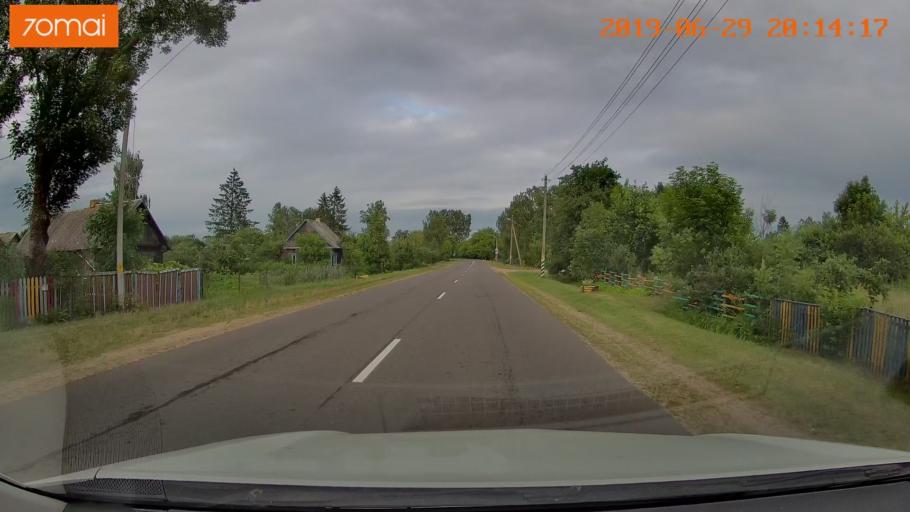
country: BY
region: Brest
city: Lahishyn
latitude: 52.3670
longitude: 26.1559
